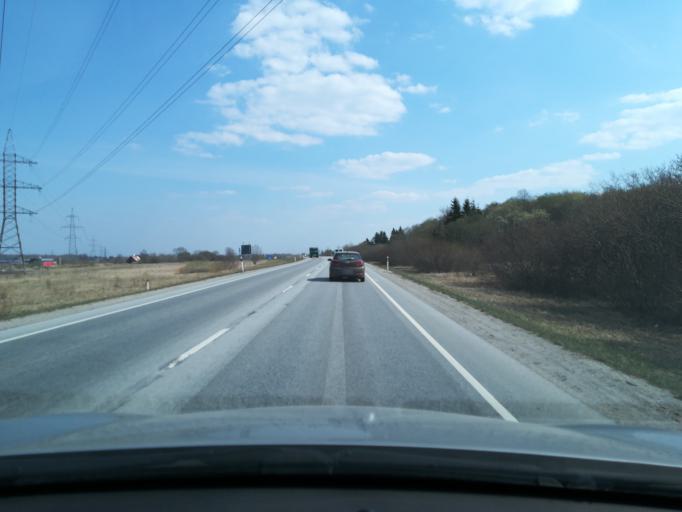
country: EE
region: Harju
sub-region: Harku vald
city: Tabasalu
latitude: 59.3907
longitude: 24.5703
